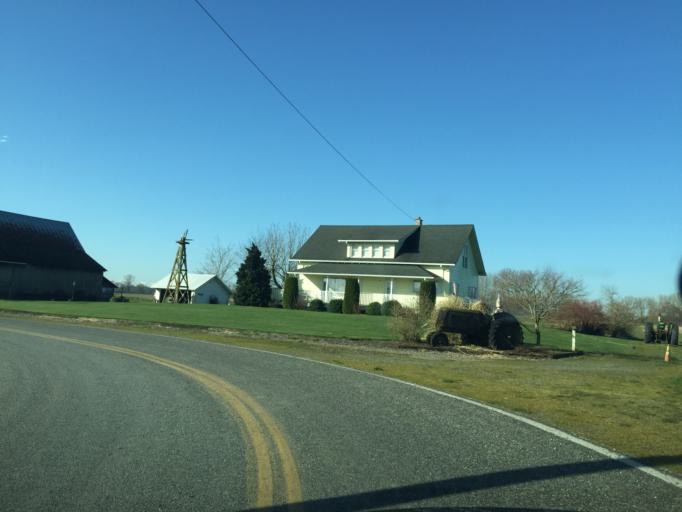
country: US
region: Washington
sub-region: Whatcom County
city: Lynden
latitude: 48.9313
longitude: -122.4561
